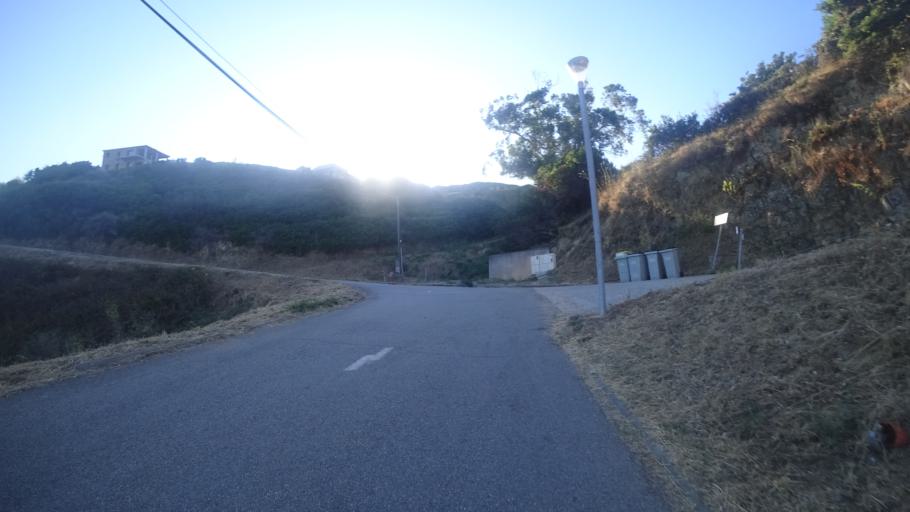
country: FR
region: Corsica
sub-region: Departement de la Corse-du-Sud
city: Alata
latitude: 41.9787
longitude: 8.6691
